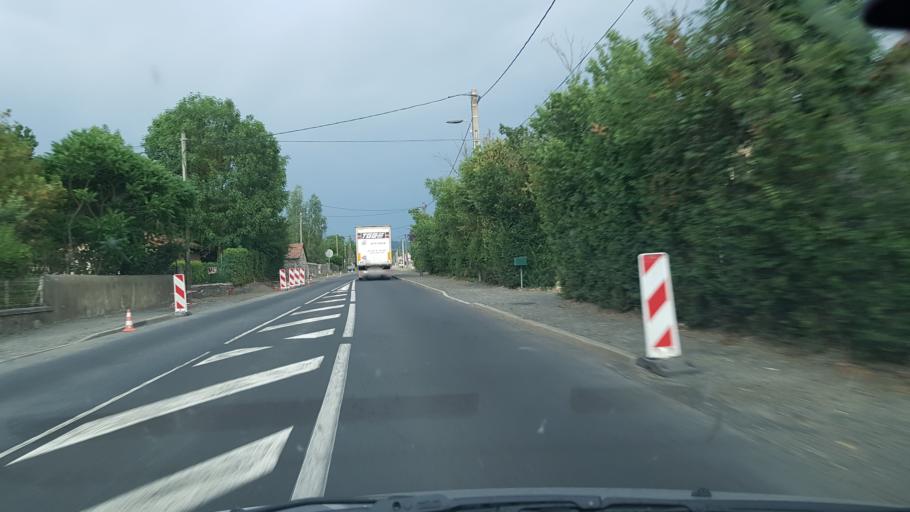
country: FR
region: Auvergne
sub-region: Departement de la Haute-Loire
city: Paulhaguet
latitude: 45.1539
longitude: 3.5434
